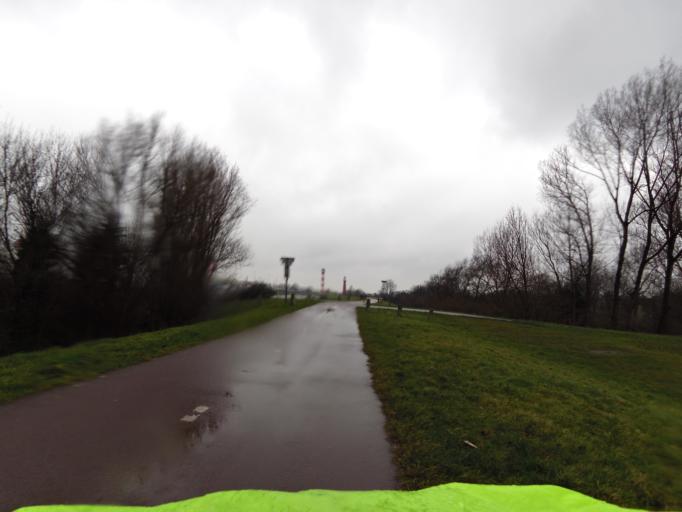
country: NL
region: South Holland
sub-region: Gemeente Rotterdam
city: Hoek van Holland
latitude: 51.9723
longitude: 4.1381
